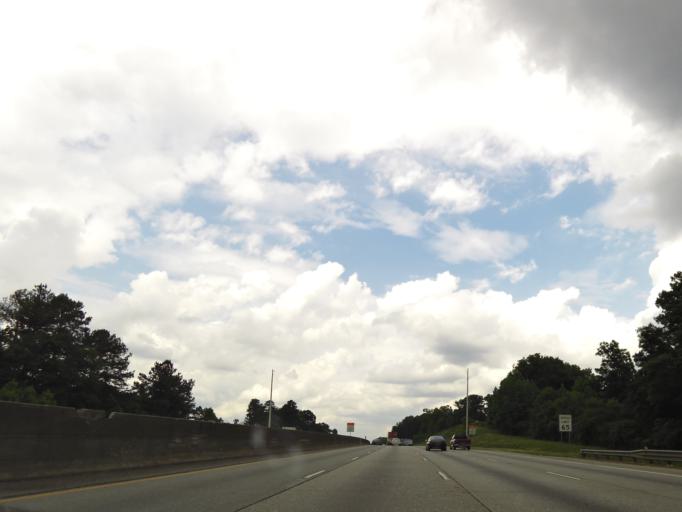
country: US
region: Georgia
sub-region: Fulton County
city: College Park
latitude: 33.6666
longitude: -84.4977
